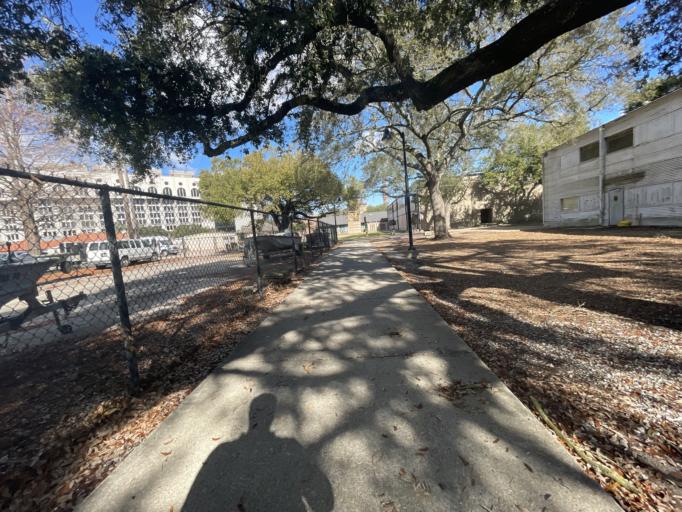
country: US
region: Louisiana
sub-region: East Baton Rouge Parish
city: Baton Rouge
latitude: 30.4090
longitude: -91.1826
